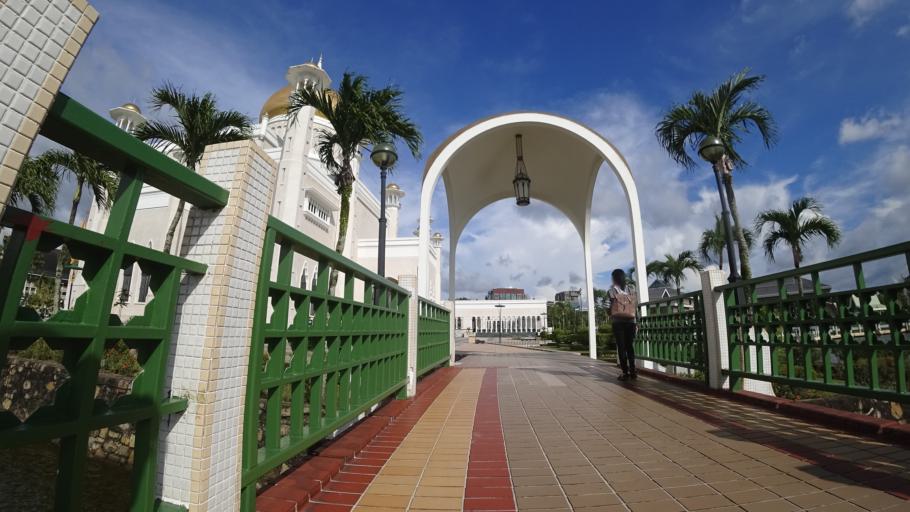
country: BN
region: Brunei and Muara
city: Bandar Seri Begawan
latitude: 4.8893
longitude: 114.9386
